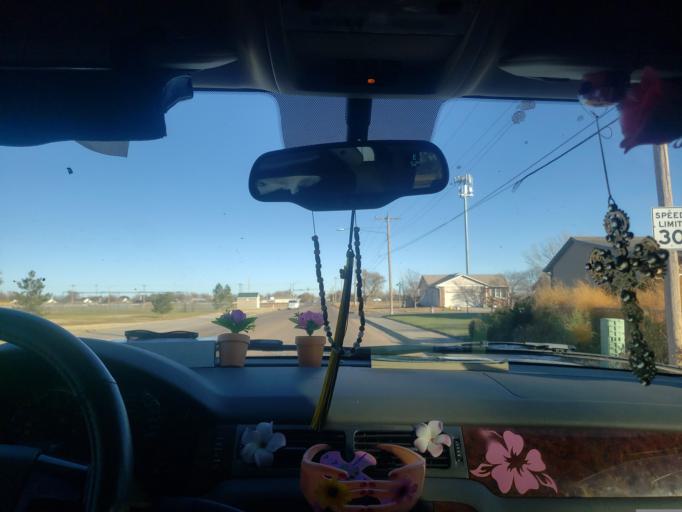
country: US
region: Kansas
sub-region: Finney County
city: Garden City
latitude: 37.9676
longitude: -100.8422
